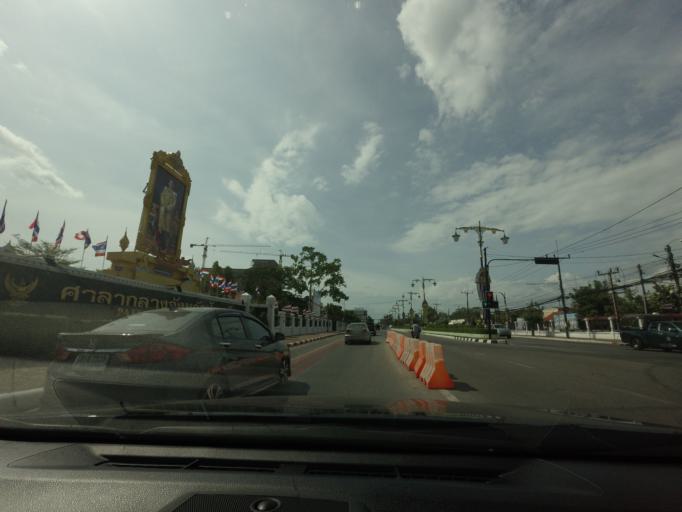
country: TH
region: Pattani
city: Pattani
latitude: 6.8679
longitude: 101.2508
